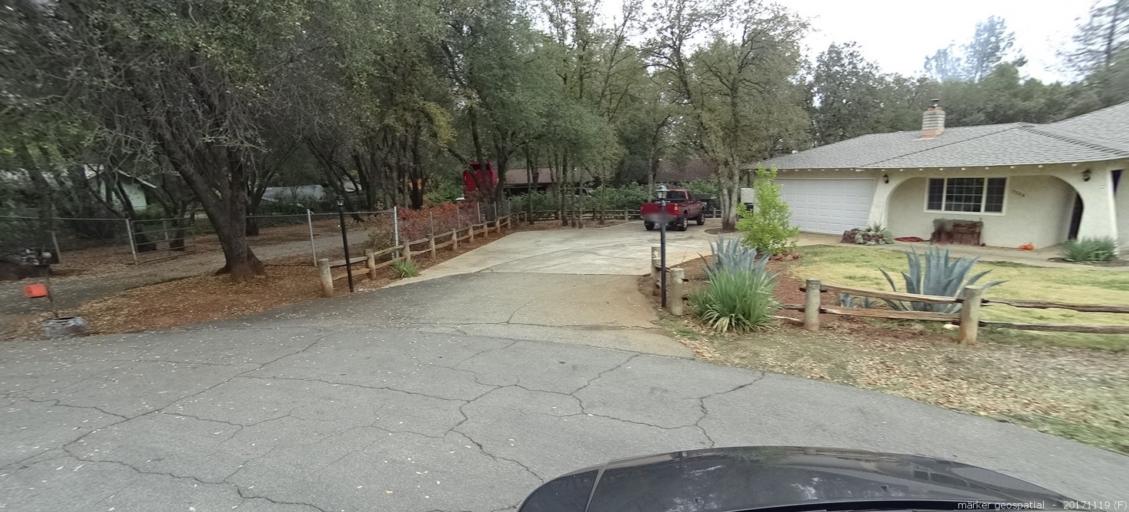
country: US
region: California
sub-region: Shasta County
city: Redding
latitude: 40.4880
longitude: -122.4191
